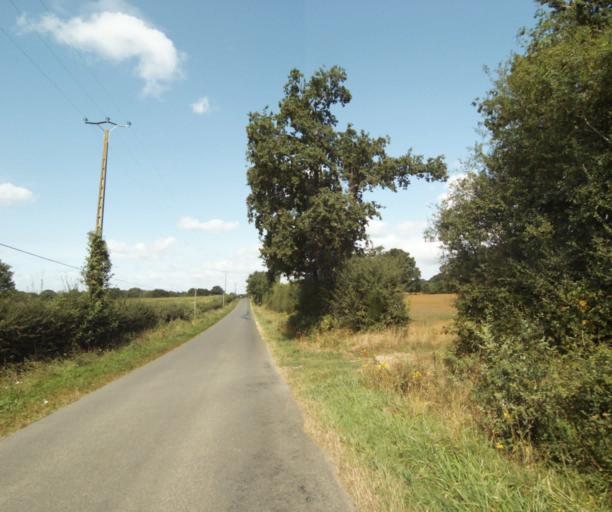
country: FR
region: Pays de la Loire
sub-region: Departement de la Sarthe
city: Sable-sur-Sarthe
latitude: 47.8515
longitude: -0.4006
